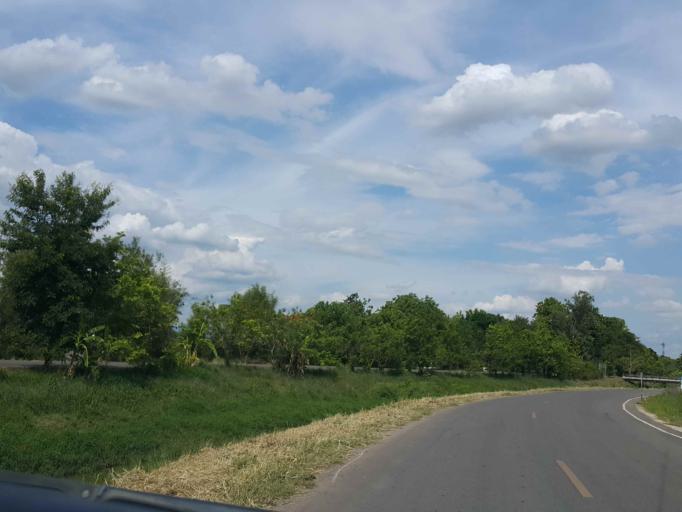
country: TH
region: Chiang Mai
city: San Sai
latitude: 18.9234
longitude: 98.9352
